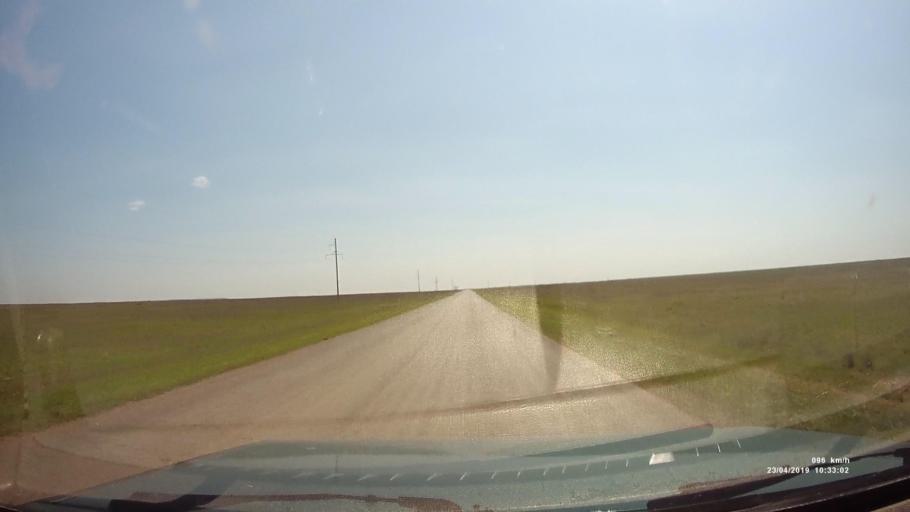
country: RU
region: Kalmykiya
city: Yashalta
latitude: 46.5762
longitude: 42.5891
